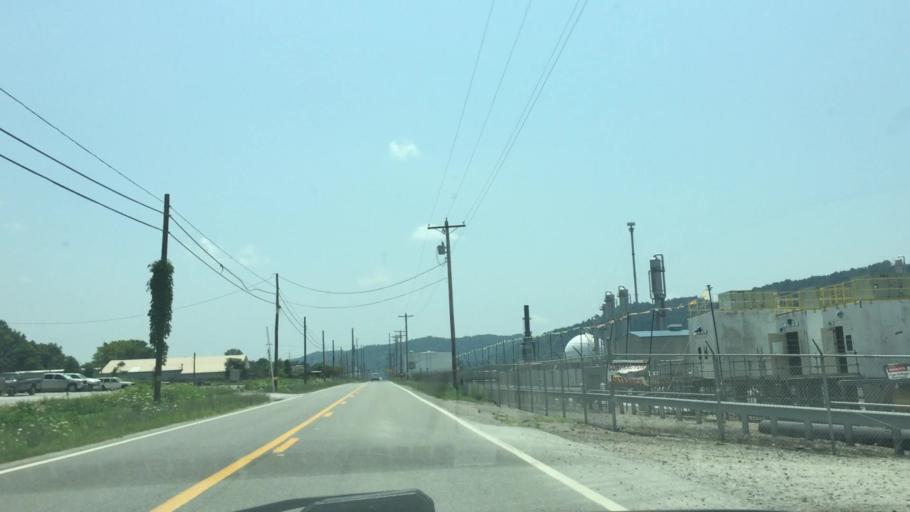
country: US
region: Ohio
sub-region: Belmont County
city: Powhatan Point
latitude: 39.7633
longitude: -80.8610
